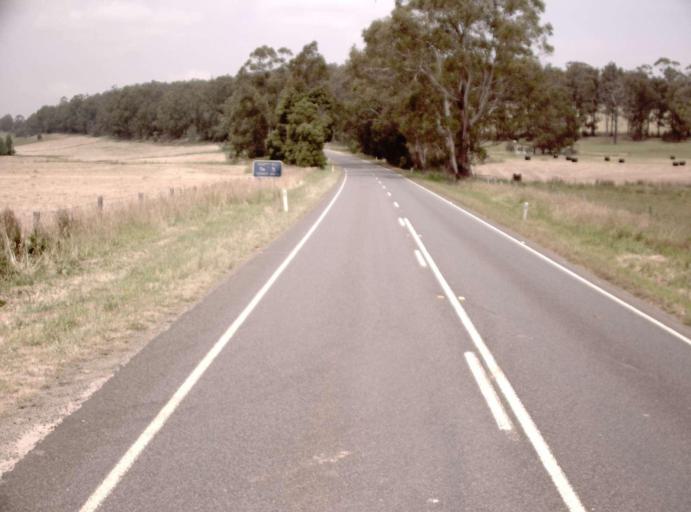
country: AU
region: Victoria
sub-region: Latrobe
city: Traralgon
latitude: -38.4370
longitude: 146.7324
